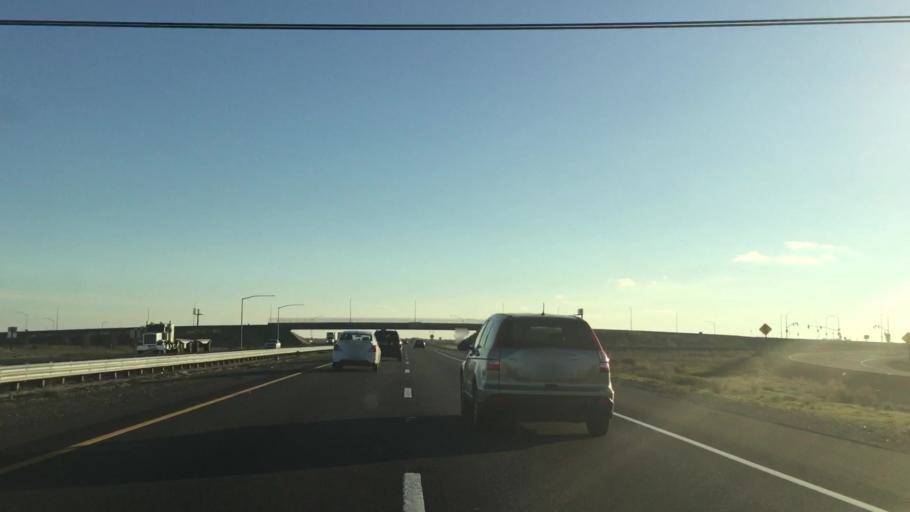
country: US
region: California
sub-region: Sacramento County
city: Elverta
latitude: 38.7178
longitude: -121.5405
